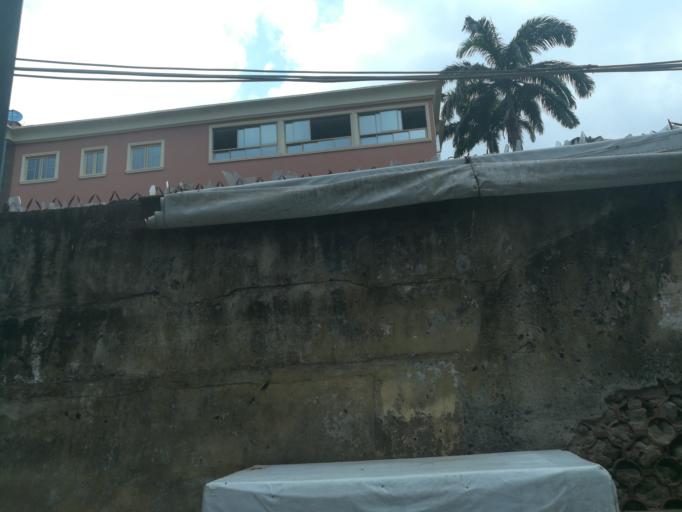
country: NG
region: Lagos
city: Ojota
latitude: 6.6030
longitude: 3.3653
